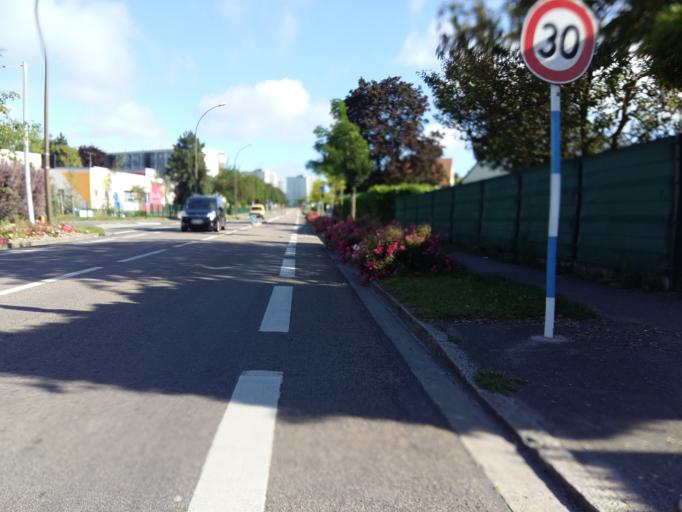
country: FR
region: Picardie
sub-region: Departement de la Somme
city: Rivery
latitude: 49.9102
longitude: 2.3254
